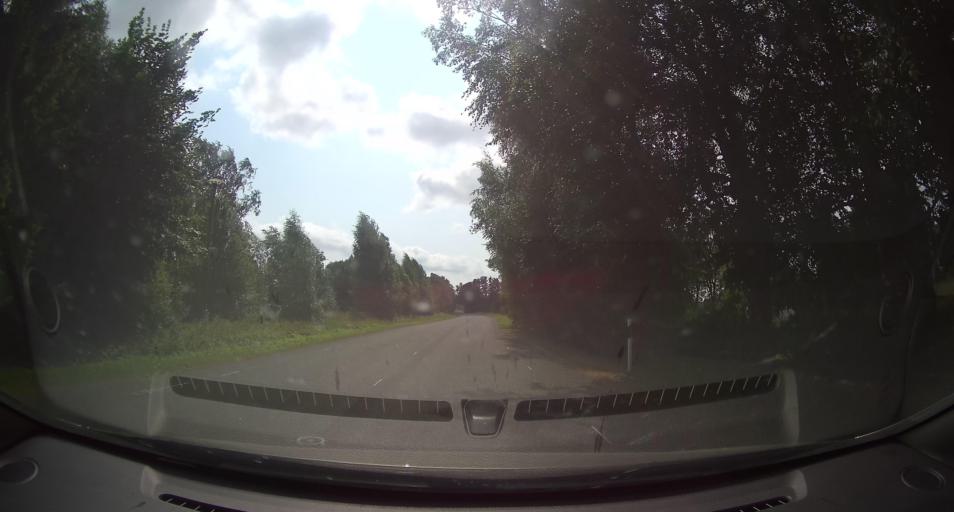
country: EE
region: Paernumaa
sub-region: Audru vald
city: Audru
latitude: 58.4946
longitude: 24.3359
